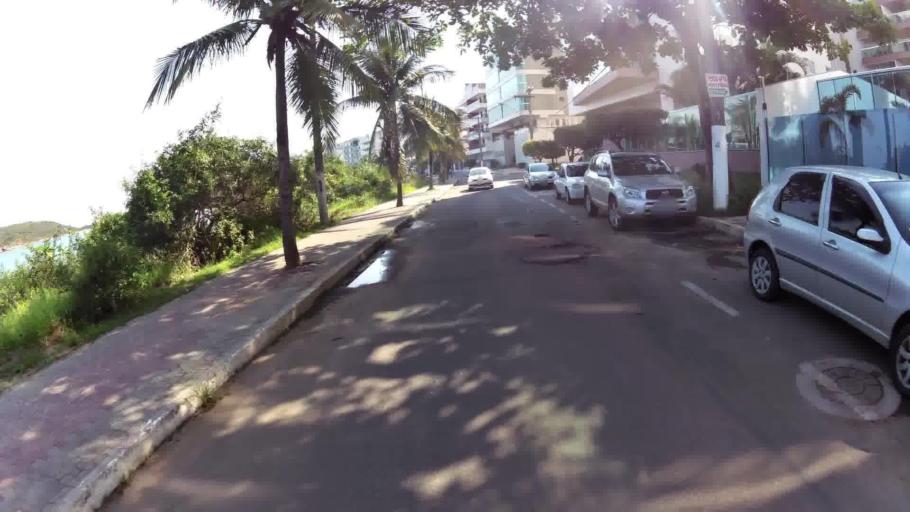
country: BR
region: Espirito Santo
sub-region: Guarapari
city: Guarapari
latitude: -20.7283
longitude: -40.5262
